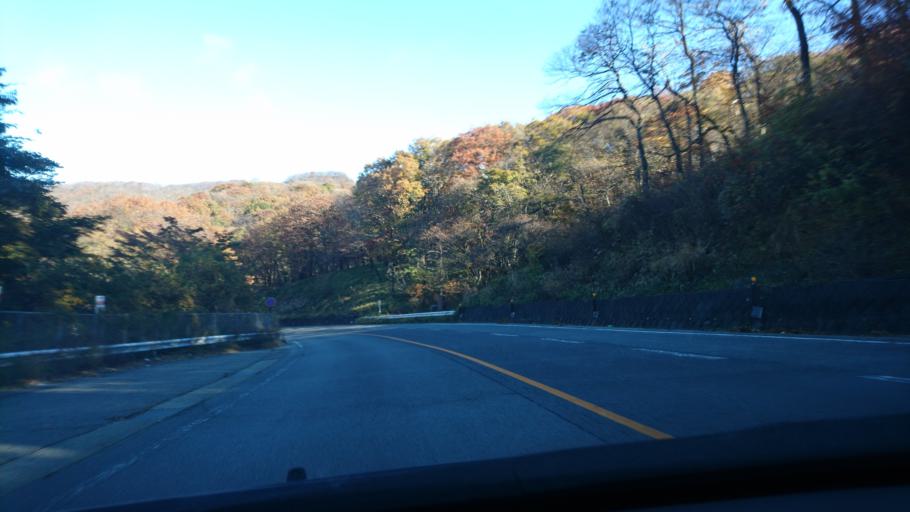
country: JP
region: Nagano
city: Saku
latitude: 36.3243
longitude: 138.6486
